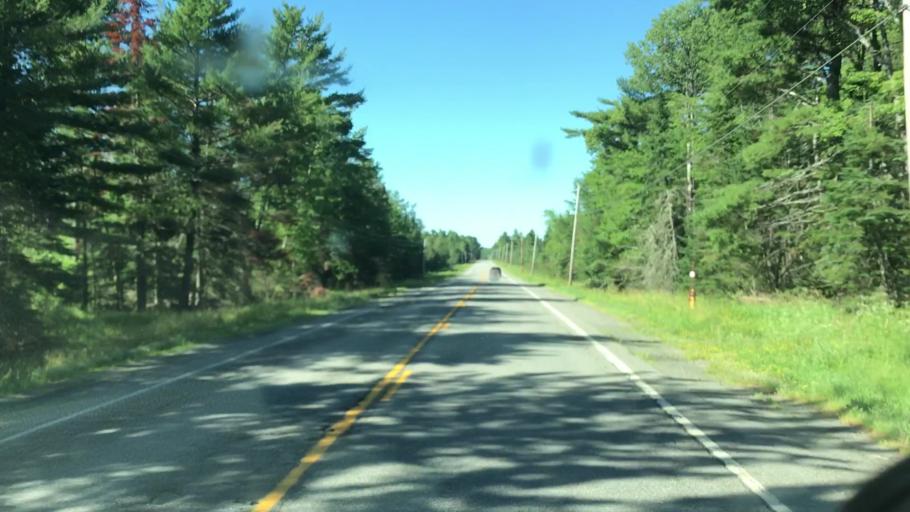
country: US
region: Maine
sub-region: Penobscot County
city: Howland
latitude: 45.2849
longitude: -68.6266
